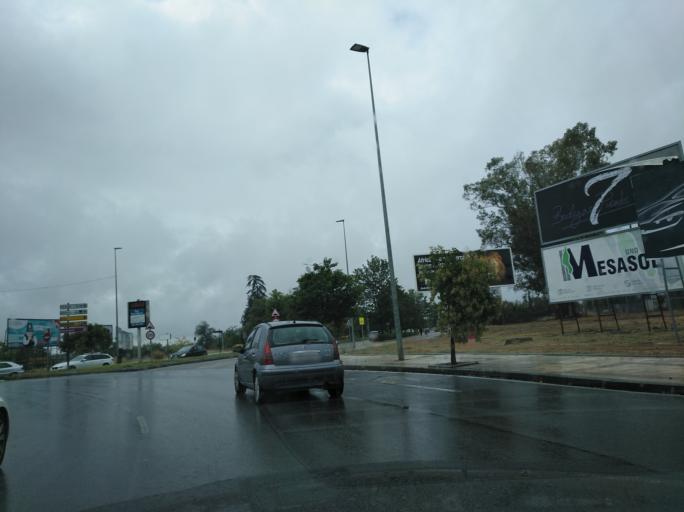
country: ES
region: Extremadura
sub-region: Provincia de Badajoz
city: Badajoz
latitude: 38.8830
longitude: -6.9980
